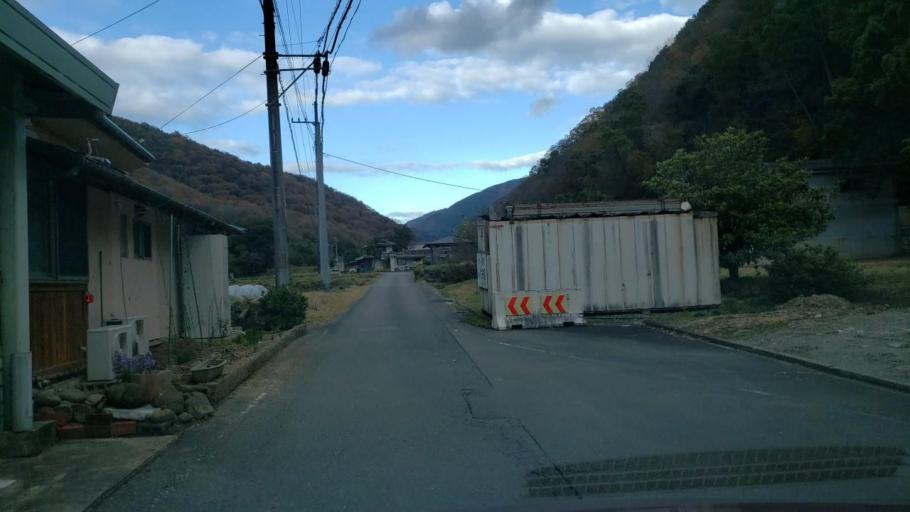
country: JP
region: Tokushima
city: Wakimachi
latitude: 34.1085
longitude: 134.2240
